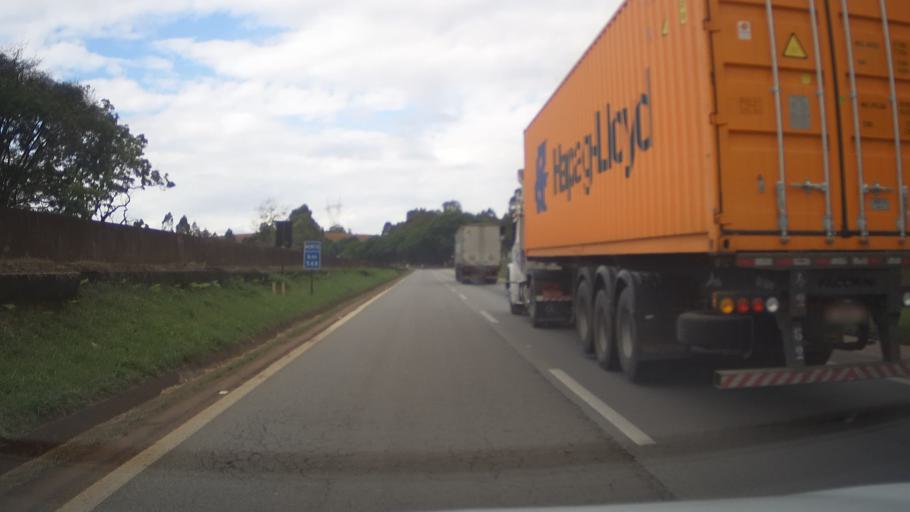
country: BR
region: Minas Gerais
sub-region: Igarape
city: Igarape
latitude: -20.2844
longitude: -44.4322
